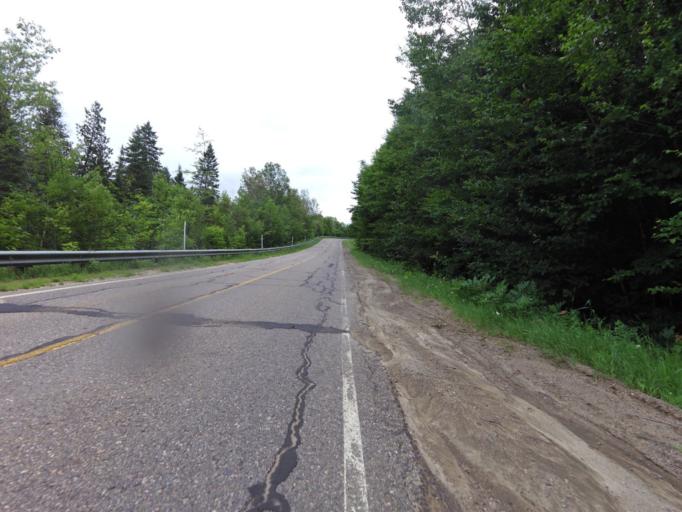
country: CA
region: Quebec
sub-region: Laurentides
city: Brownsburg-Chatham
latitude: 45.8916
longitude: -74.5934
